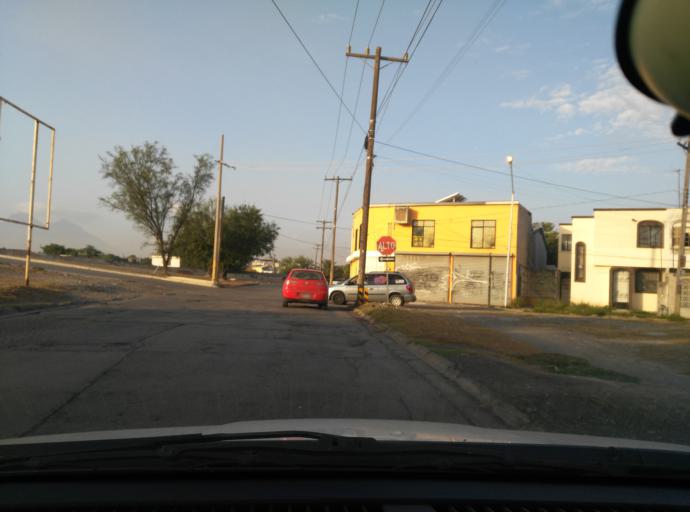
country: MX
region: Nuevo Leon
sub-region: San Nicolas de los Garza
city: San Nicolas de los Garza
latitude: 25.7602
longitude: -100.2520
